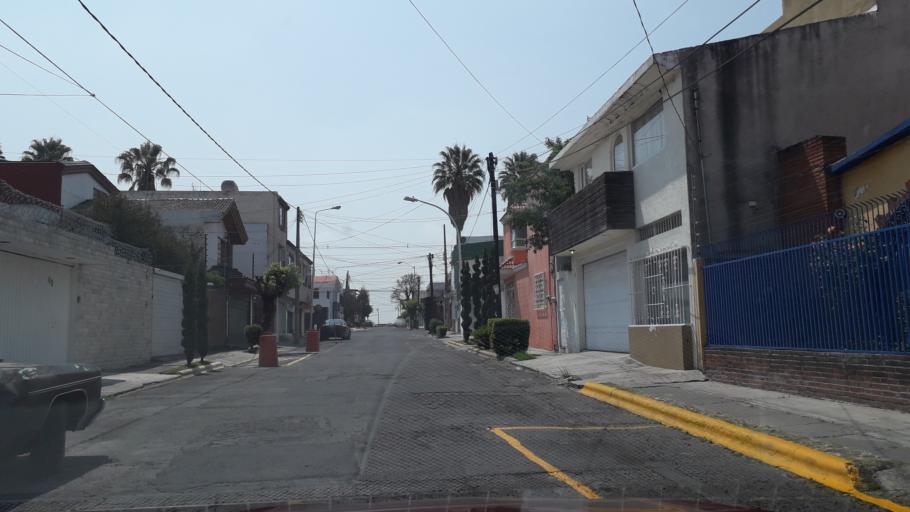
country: MX
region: Puebla
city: Puebla
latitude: 19.0580
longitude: -98.1784
